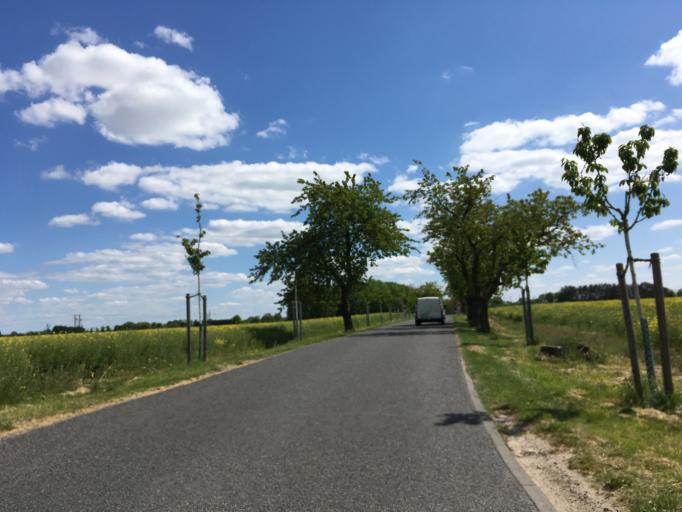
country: DE
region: Brandenburg
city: Biesenthal
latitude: 52.7415
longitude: 13.6555
